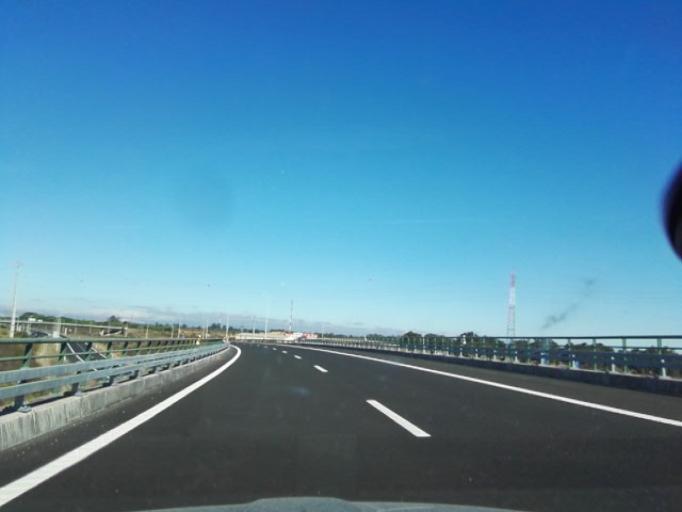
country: PT
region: Santarem
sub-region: Benavente
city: Poceirao
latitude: 38.9066
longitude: -8.7833
